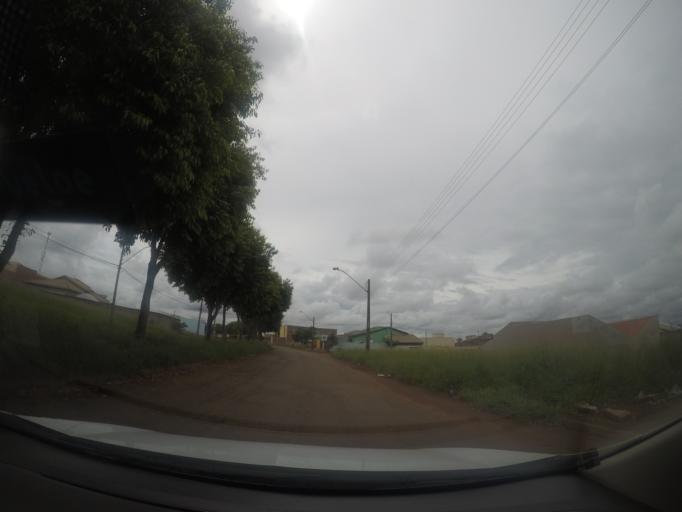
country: BR
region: Goias
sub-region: Trindade
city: Trindade
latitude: -16.6916
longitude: -49.3905
